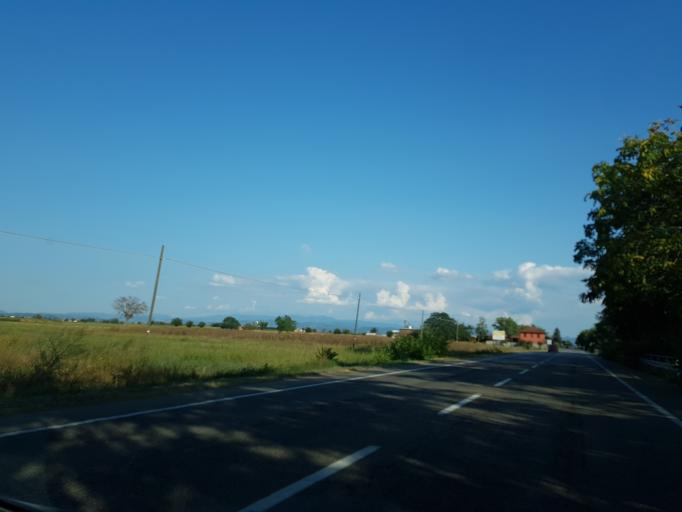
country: IT
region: Piedmont
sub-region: Provincia di Alessandria
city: Litta Parodi-Cascinagrossa
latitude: 44.8585
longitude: 8.7110
